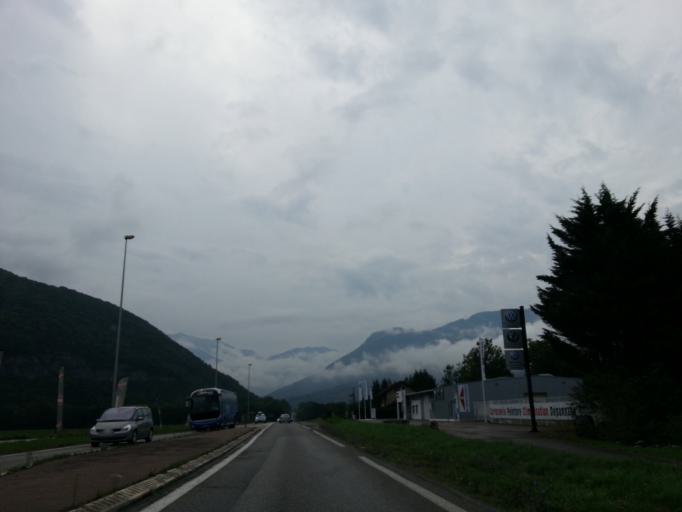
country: FR
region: Rhone-Alpes
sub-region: Departement de la Haute-Savoie
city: Doussard
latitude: 45.7775
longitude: 6.2335
